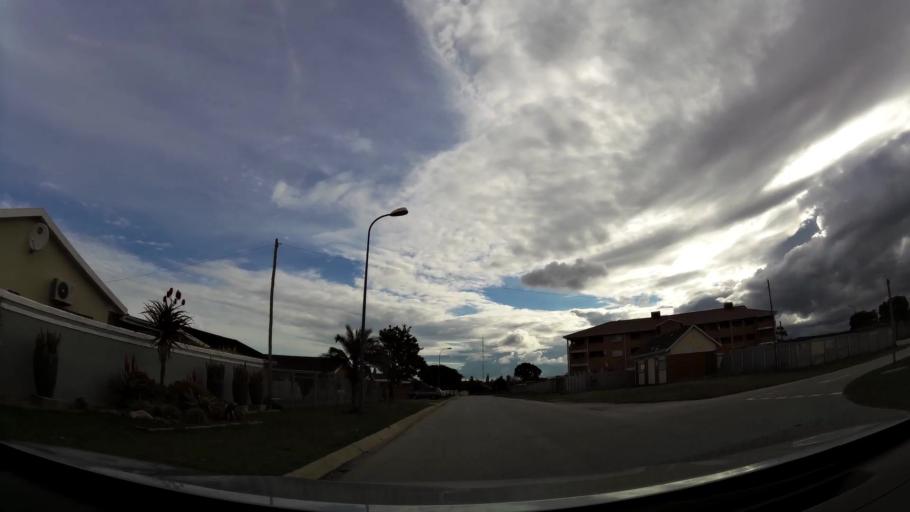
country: ZA
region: Eastern Cape
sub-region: Nelson Mandela Bay Metropolitan Municipality
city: Port Elizabeth
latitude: -33.9381
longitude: 25.4620
